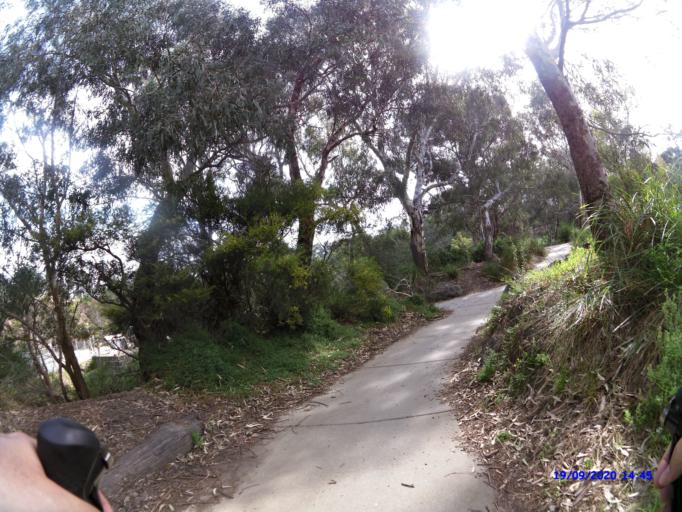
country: AU
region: Victoria
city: Abbotsford
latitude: -37.7966
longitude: 145.0013
